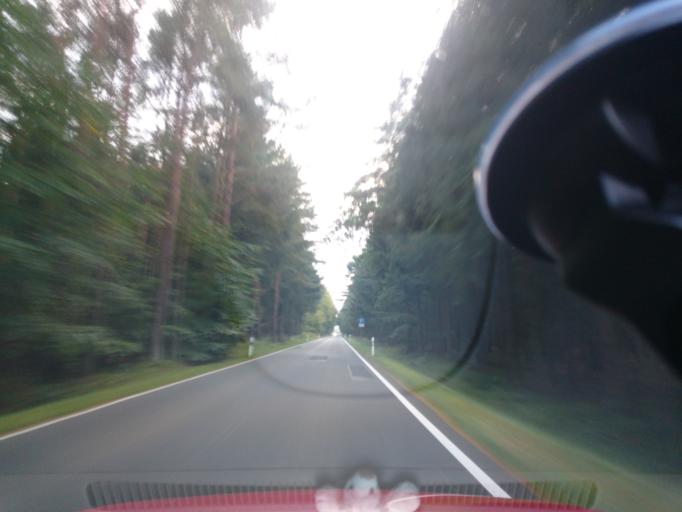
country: DE
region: Mecklenburg-Vorpommern
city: Born
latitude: 54.3398
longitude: 12.5573
